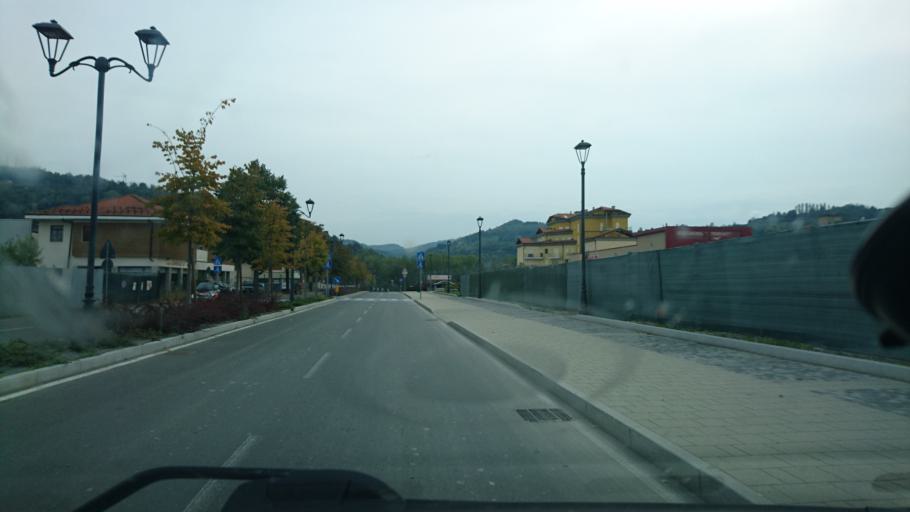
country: IT
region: Piedmont
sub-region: Provincia di Alessandria
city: Acqui Terme
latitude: 44.6688
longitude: 8.4710
